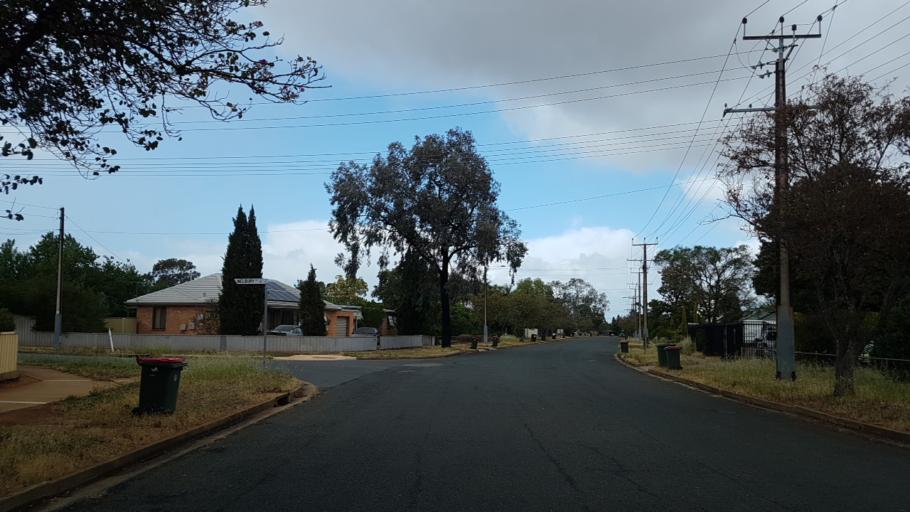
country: AU
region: South Australia
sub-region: Playford
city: Smithfield
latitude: -34.6920
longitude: 138.6639
